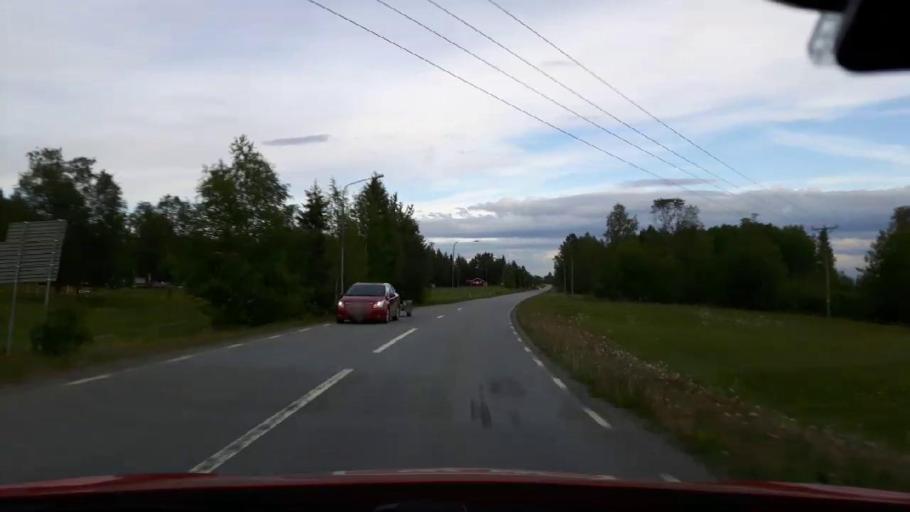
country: SE
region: Jaemtland
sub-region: Bergs Kommun
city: Hoverberg
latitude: 62.9739
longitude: 14.4850
